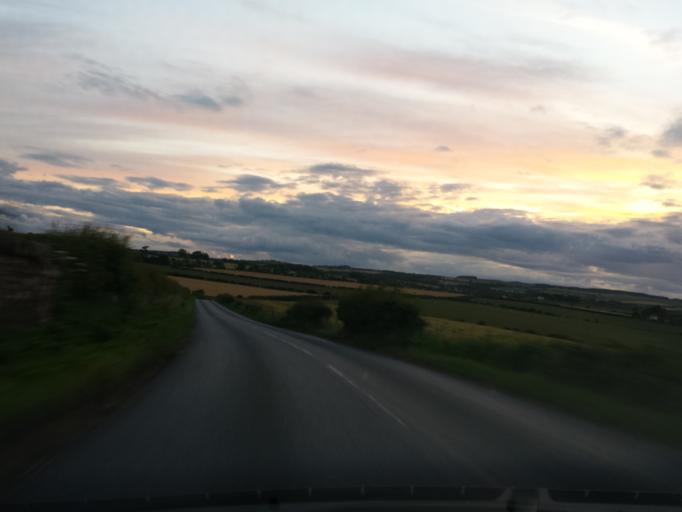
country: GB
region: Scotland
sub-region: The Scottish Borders
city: Eyemouth
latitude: 55.8758
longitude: -2.1250
